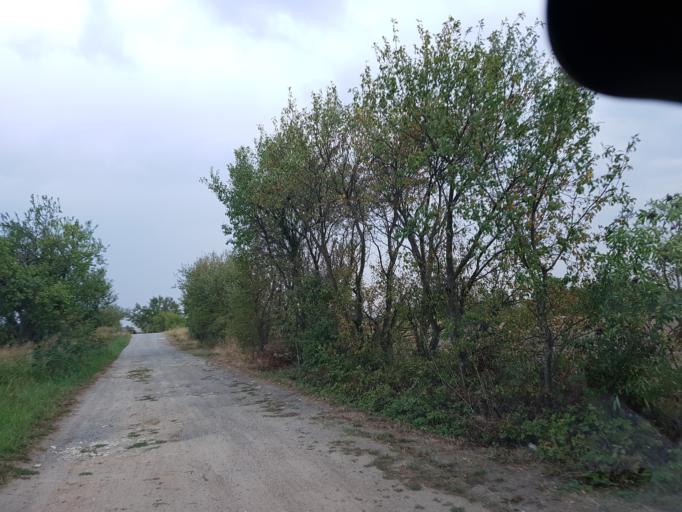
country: DE
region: Brandenburg
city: Herzberg
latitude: 51.7028
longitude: 13.2630
